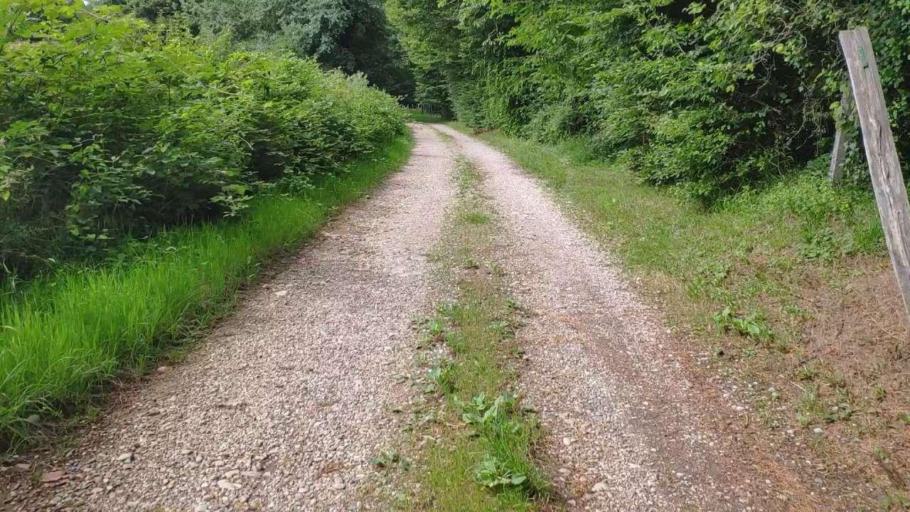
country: FR
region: Franche-Comte
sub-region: Departement du Jura
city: Bletterans
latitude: 46.8068
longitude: 5.4469
